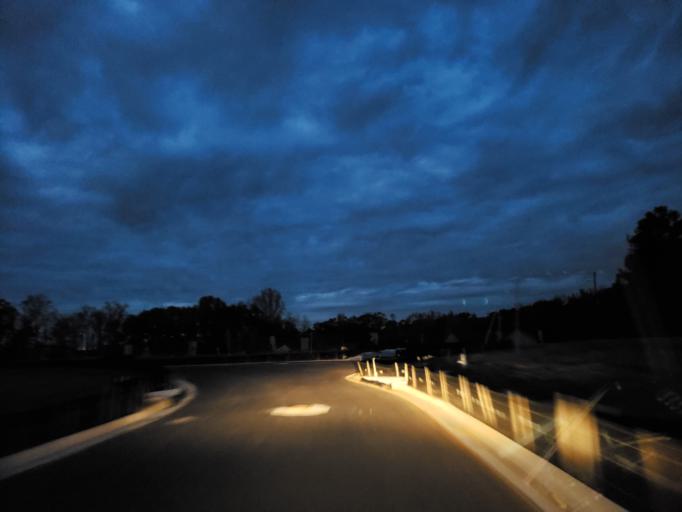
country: US
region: Georgia
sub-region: Cobb County
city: Powder Springs
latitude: 33.8808
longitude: -84.7157
